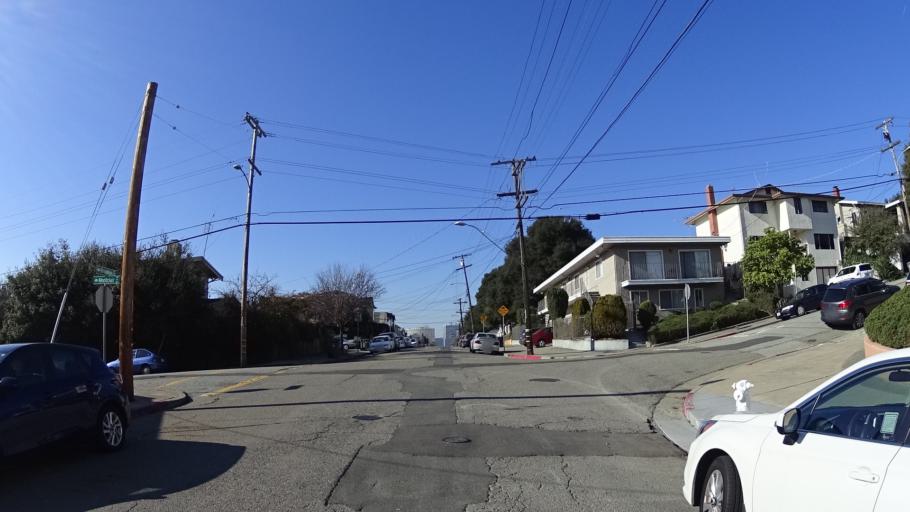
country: US
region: California
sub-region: Alameda County
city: Piedmont
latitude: 37.8028
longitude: -122.2434
